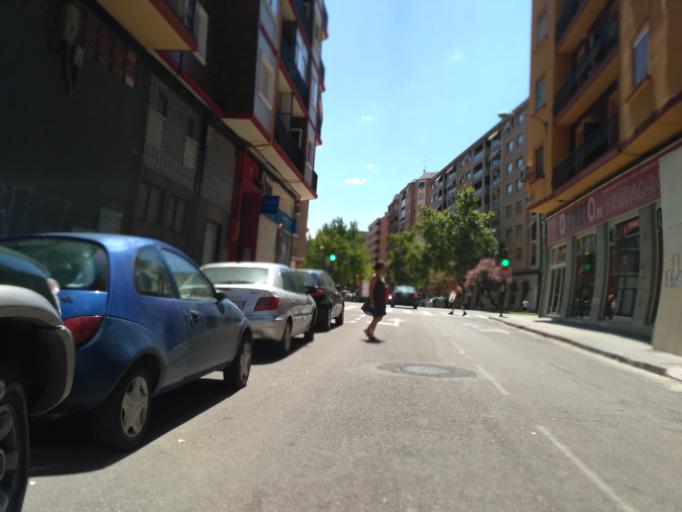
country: ES
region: Aragon
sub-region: Provincia de Zaragoza
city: Almozara
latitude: 41.6556
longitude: -0.9044
